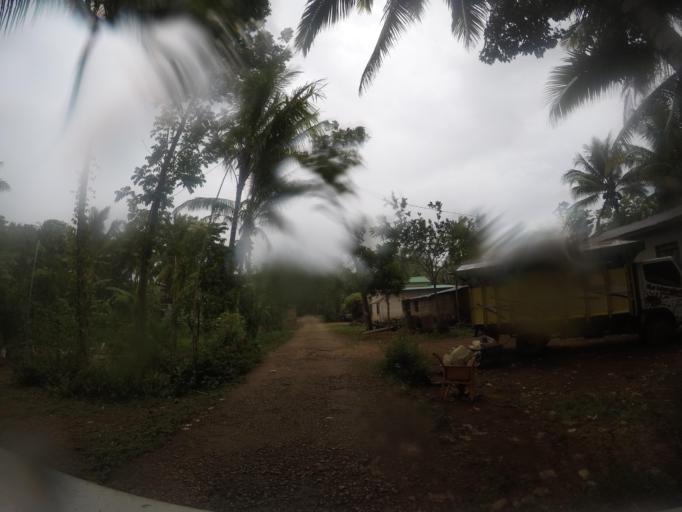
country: TL
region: Lautem
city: Lospalos
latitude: -8.5286
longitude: 126.9943
